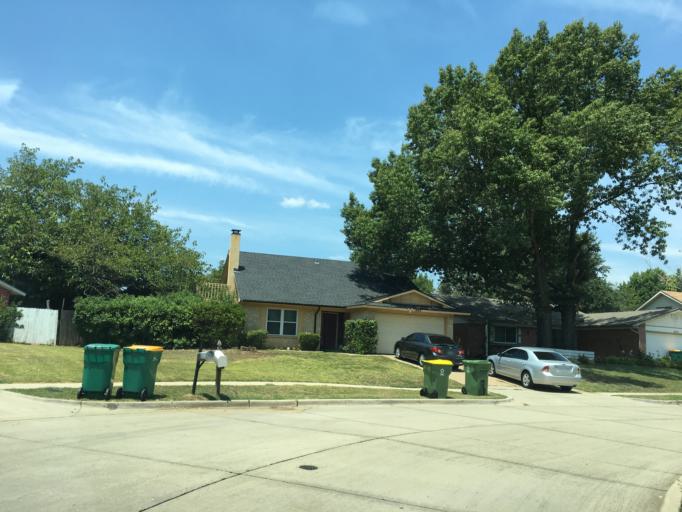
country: US
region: Texas
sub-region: Denton County
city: Lewisville
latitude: 33.0289
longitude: -97.0052
